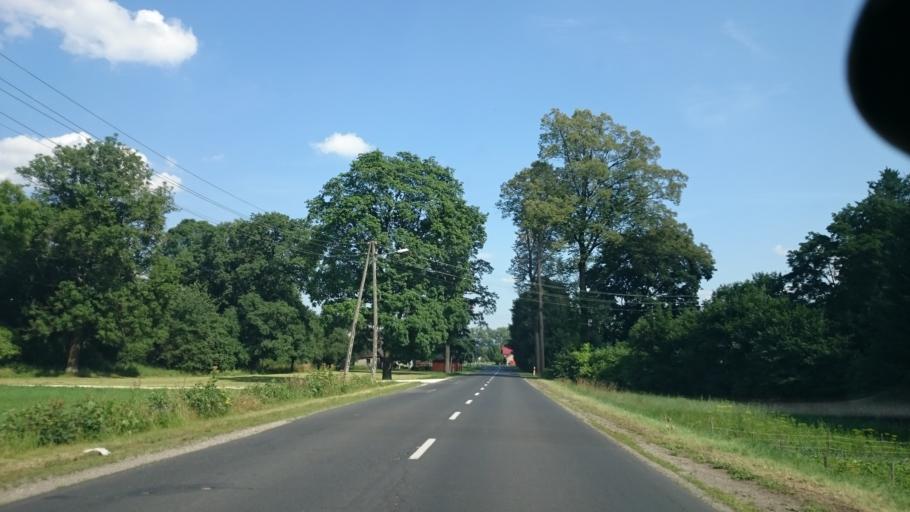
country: PL
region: Lower Silesian Voivodeship
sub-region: Powiat klodzki
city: Bystrzyca Klodzka
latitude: 50.3523
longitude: 16.7539
